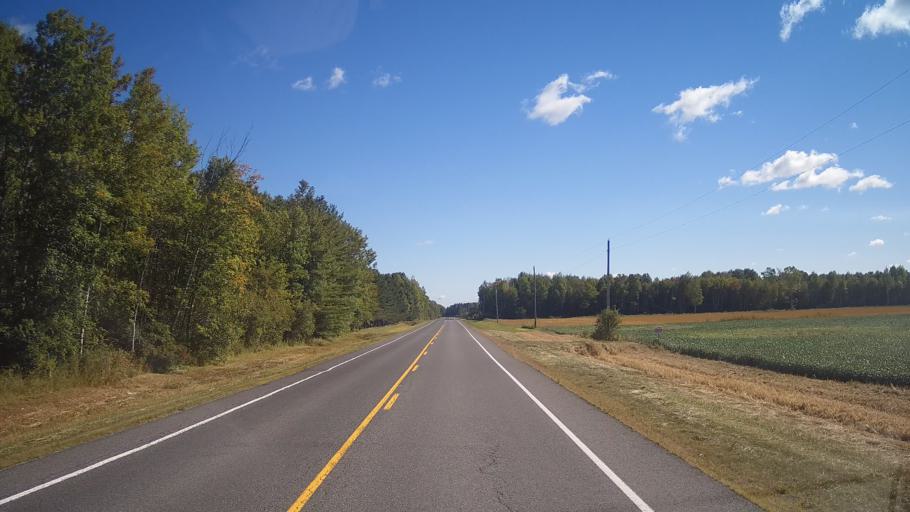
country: CA
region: Ontario
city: Prescott
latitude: 44.9131
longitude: -75.4217
